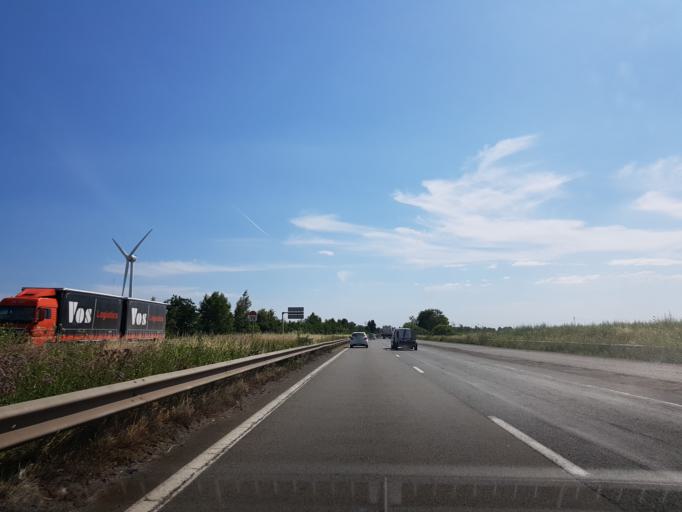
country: FR
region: Nord-Pas-de-Calais
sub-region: Departement du Nord
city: Onnaing
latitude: 50.3773
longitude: 3.6073
